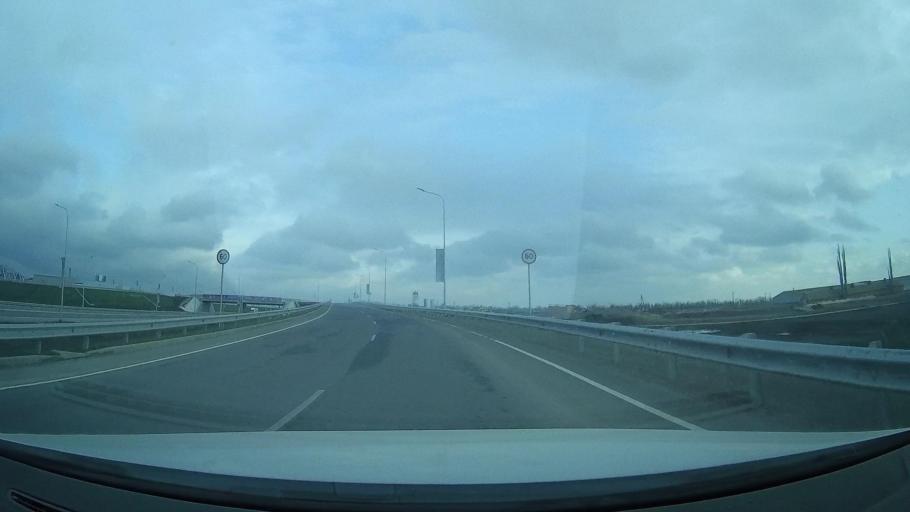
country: RU
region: Rostov
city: Grushevskaya
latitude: 47.4818
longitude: 39.9271
